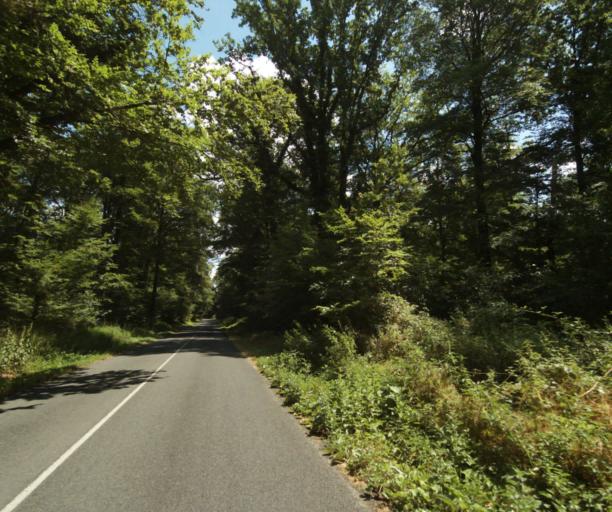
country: FR
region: Ile-de-France
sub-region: Departement de Seine-et-Marne
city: Samois-sur-Seine
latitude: 48.4535
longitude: 2.7340
